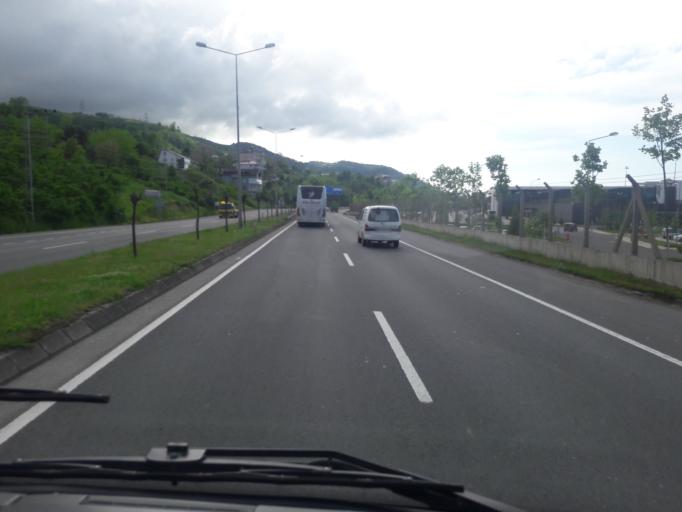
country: TR
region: Ordu
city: Gulyali
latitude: 40.9629
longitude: 38.0833
